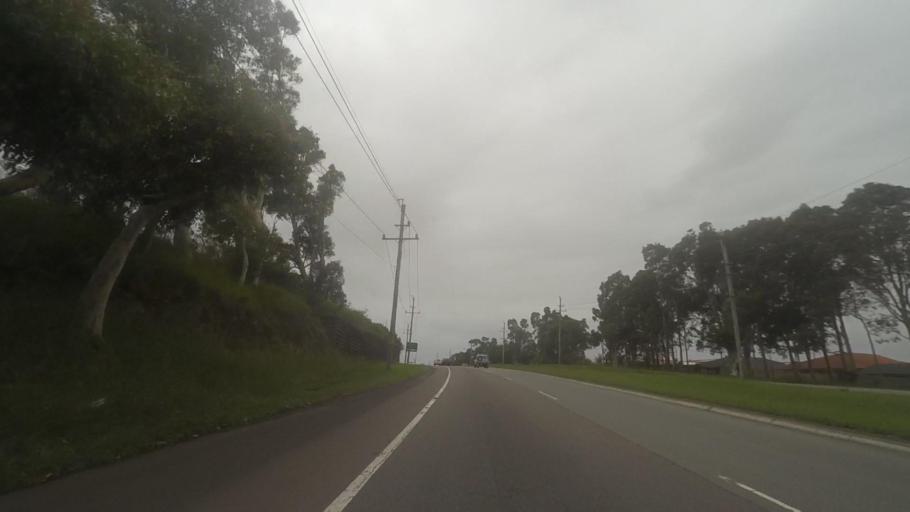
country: AU
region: New South Wales
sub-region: Newcastle
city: Mayfield West
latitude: -32.8780
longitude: 151.7150
